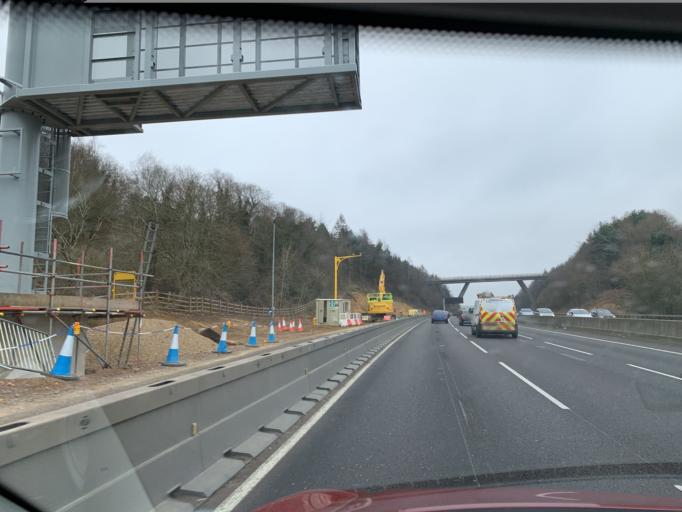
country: GB
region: England
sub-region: Surrey
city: Bletchingley
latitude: 51.2378
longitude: -0.1182
